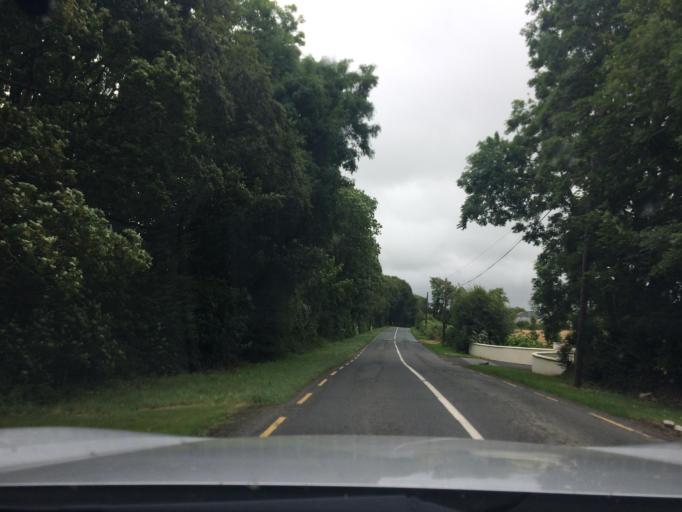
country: IE
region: Munster
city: Cashel
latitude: 52.4806
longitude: -7.8513
